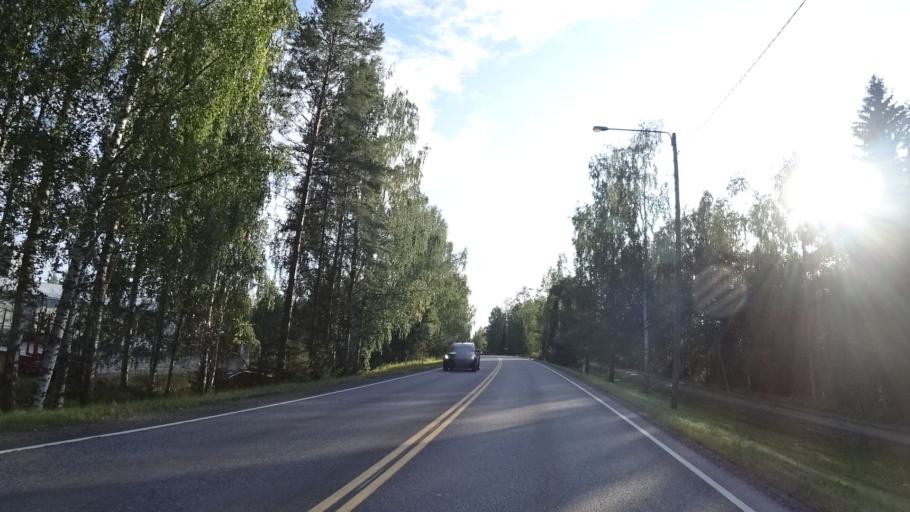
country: FI
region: South Karelia
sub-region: Imatra
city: Parikkala
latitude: 61.6059
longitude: 29.4876
